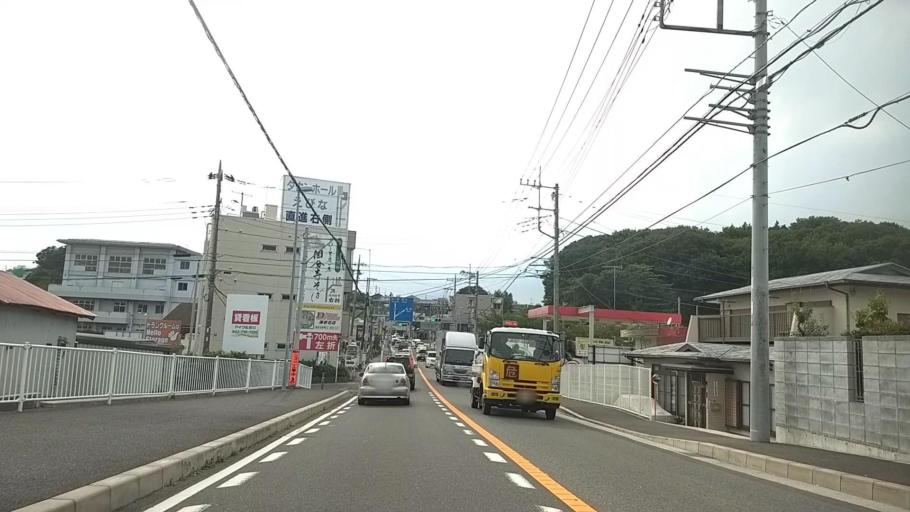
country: JP
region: Kanagawa
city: Zama
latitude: 35.4532
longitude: 139.4044
